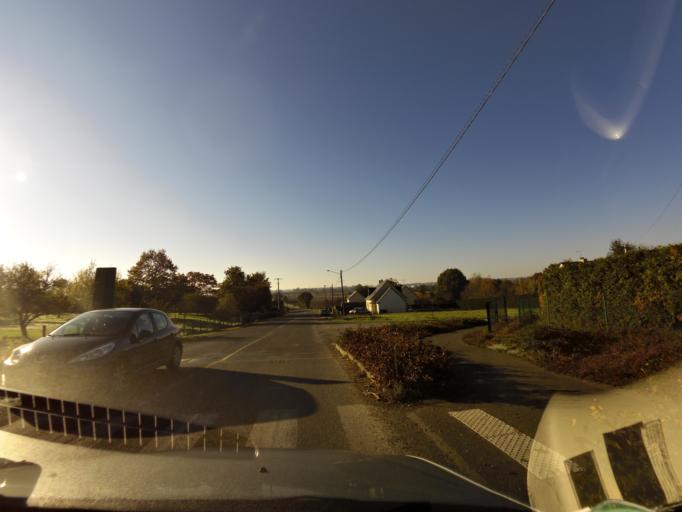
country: FR
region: Brittany
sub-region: Departement d'Ille-et-Vilaine
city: Pance
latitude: 47.8717
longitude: -1.6789
